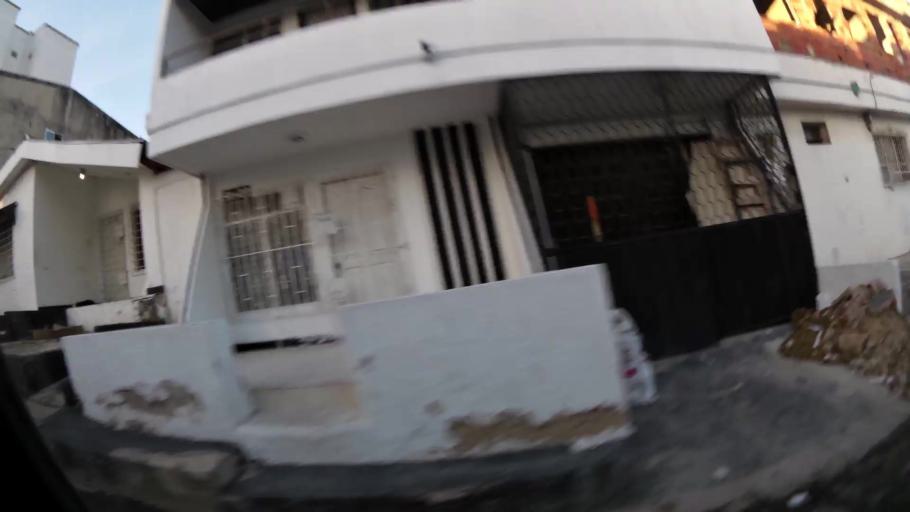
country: CO
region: Atlantico
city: Barranquilla
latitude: 10.9783
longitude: -74.7989
